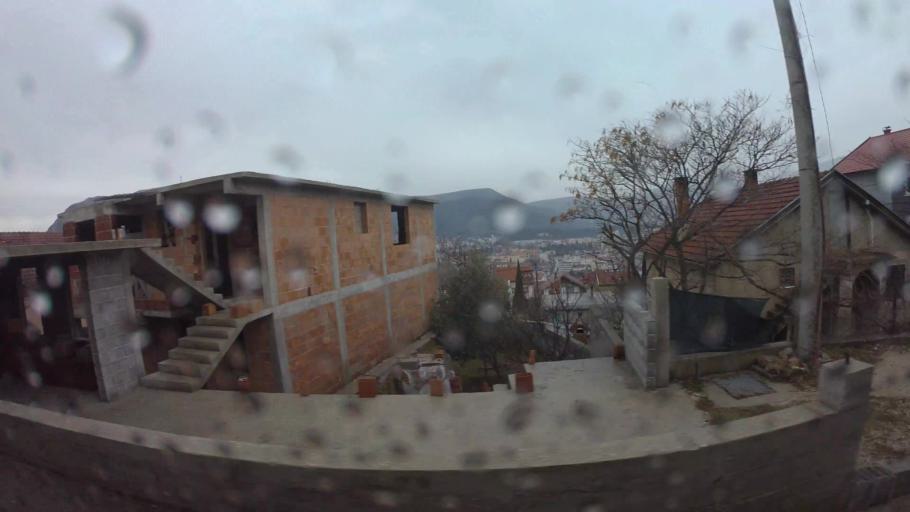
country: BA
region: Federation of Bosnia and Herzegovina
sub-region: Hercegovacko-Bosanski Kanton
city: Mostar
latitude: 43.3453
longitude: 17.8180
